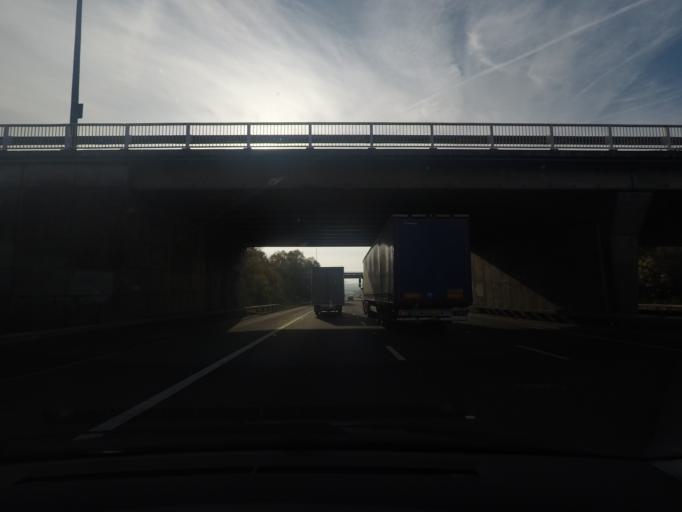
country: GB
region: England
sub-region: Barnsley
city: Dodworth
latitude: 53.5494
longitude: -1.5160
